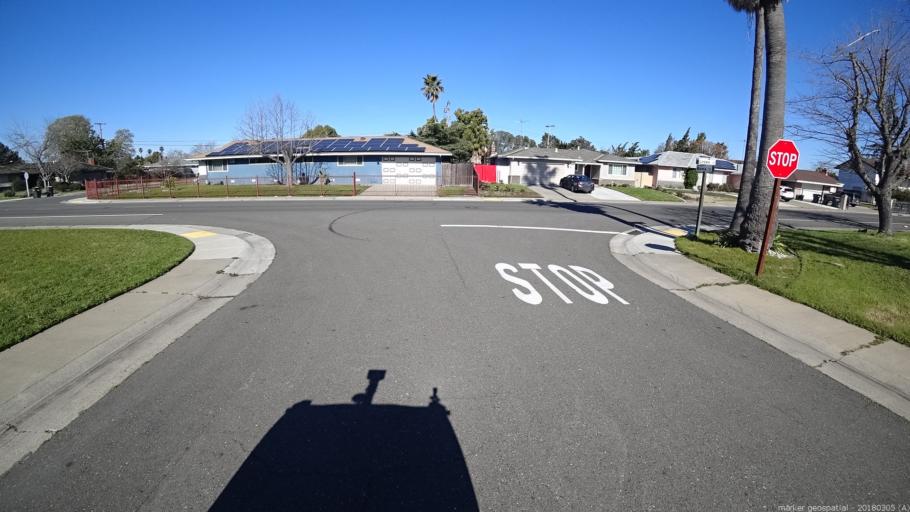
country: US
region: California
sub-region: Sacramento County
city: Florin
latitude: 38.4920
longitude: -121.4211
